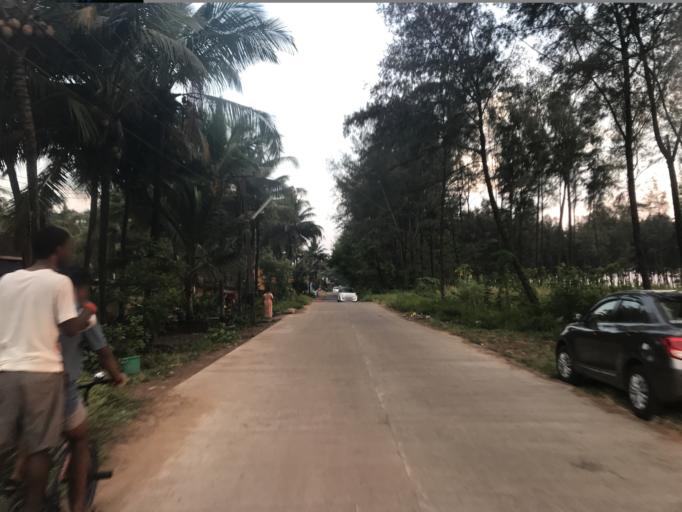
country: IN
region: Karnataka
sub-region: Dakshina Kannada
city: Mangalore
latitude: 12.8906
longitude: 74.8155
